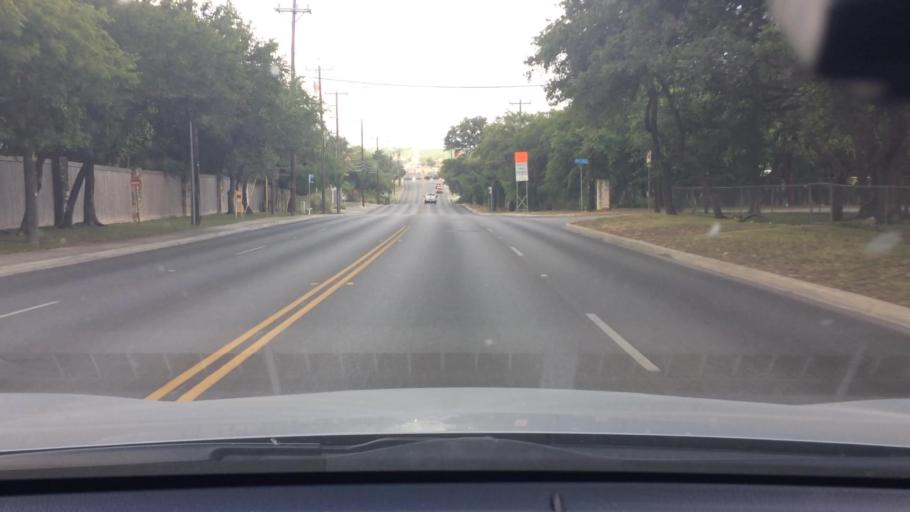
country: US
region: Texas
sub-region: Bexar County
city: Hollywood Park
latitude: 29.5605
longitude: -98.4768
